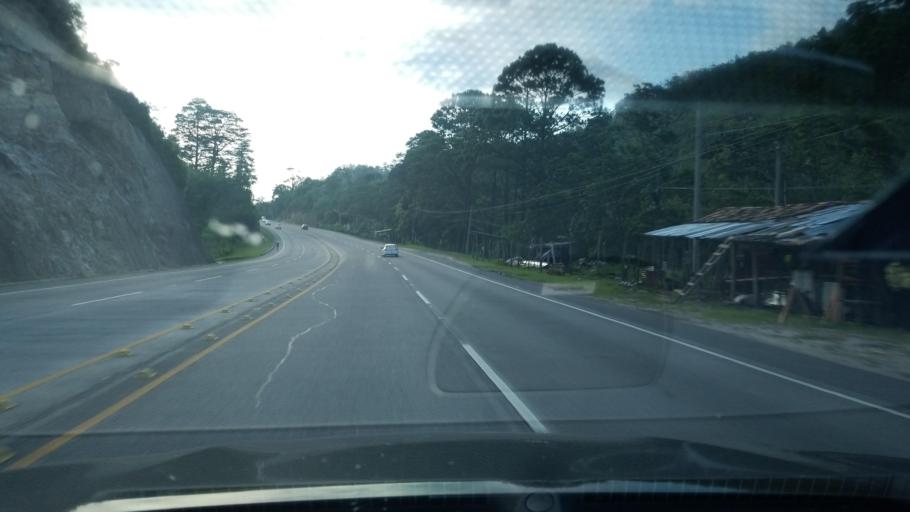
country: HN
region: Comayagua
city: El Socorro
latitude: 14.6579
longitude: -87.9428
